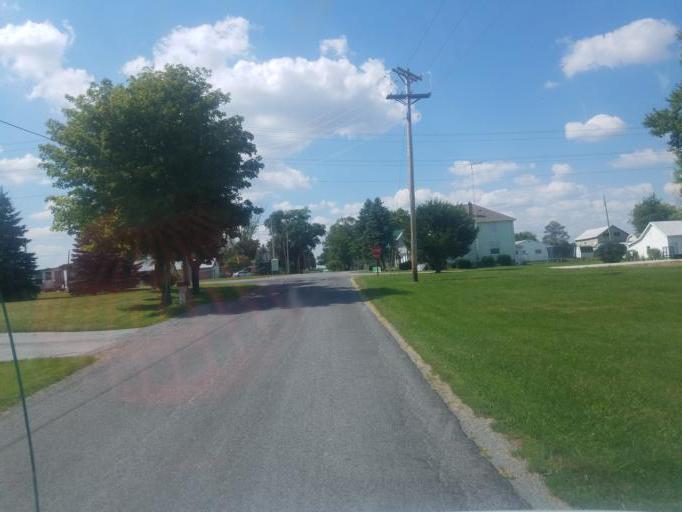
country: US
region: Ohio
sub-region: Hardin County
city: Ada
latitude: 40.6540
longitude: -83.8926
